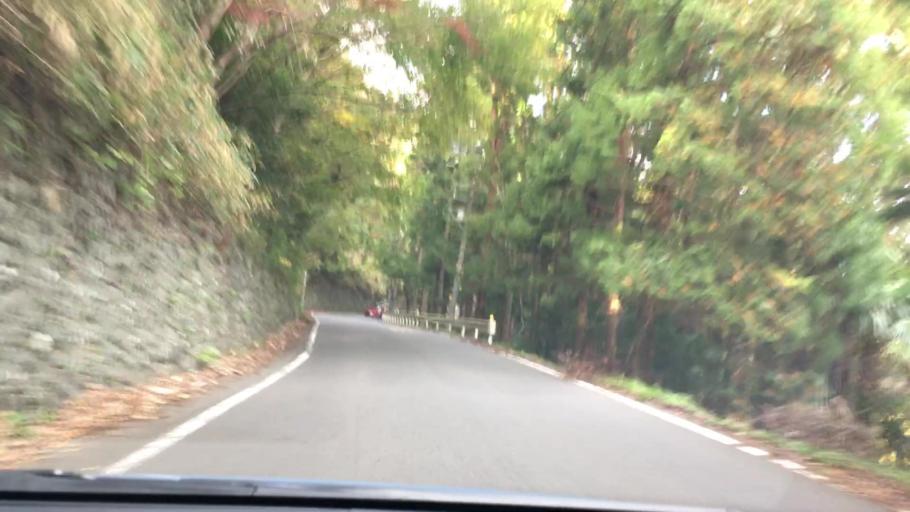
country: JP
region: Yamanashi
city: Uenohara
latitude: 35.5521
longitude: 139.1388
